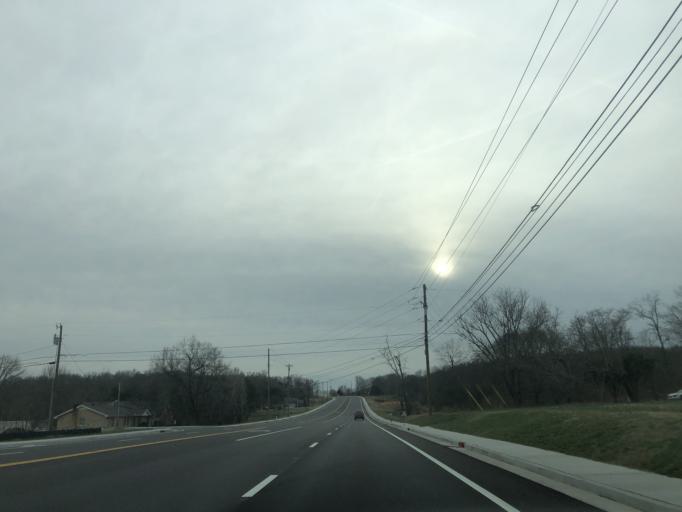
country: US
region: Tennessee
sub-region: Wilson County
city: Lebanon
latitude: 36.2412
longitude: -86.2594
